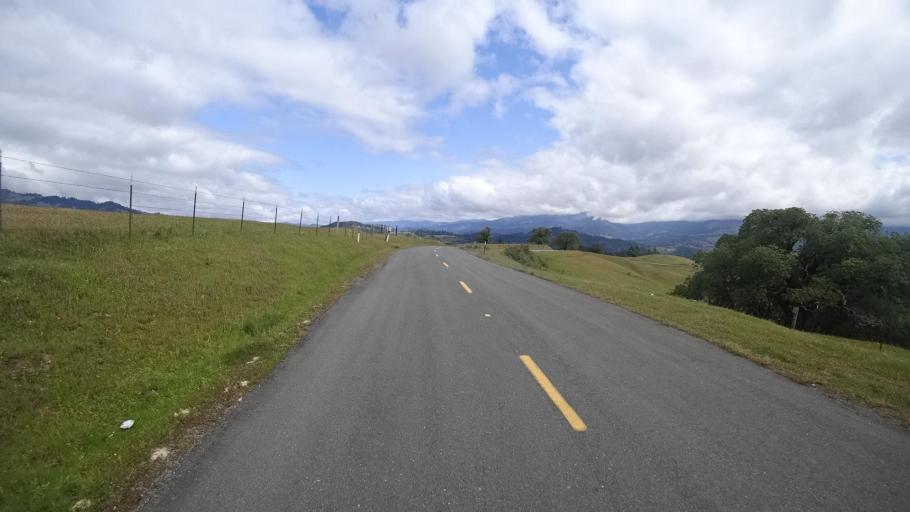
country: US
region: California
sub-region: Humboldt County
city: Redway
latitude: 40.1539
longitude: -123.6230
